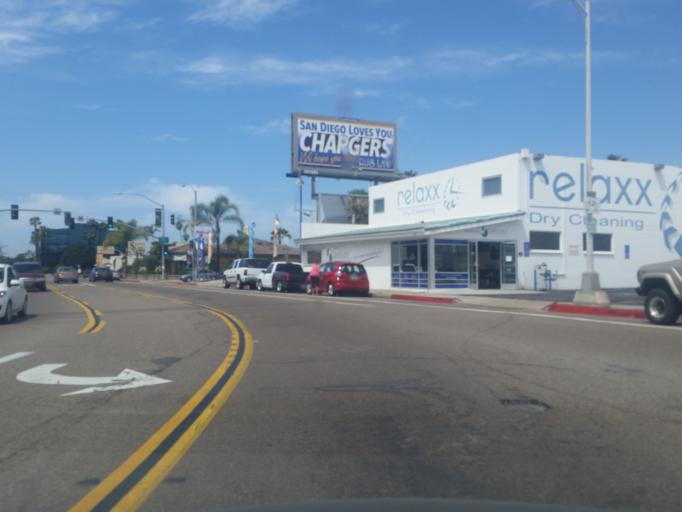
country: US
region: California
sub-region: San Diego County
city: San Diego
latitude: 32.7686
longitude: -117.1997
